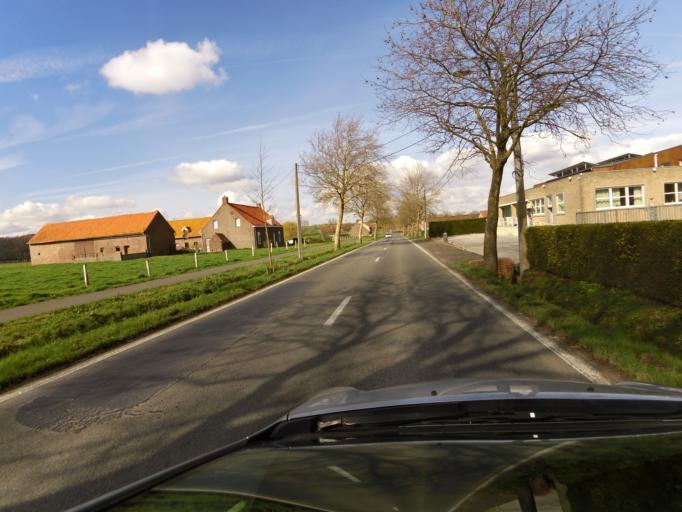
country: FR
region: Nord-Pas-de-Calais
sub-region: Departement du Nord
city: Nieppe
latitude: 50.7584
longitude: 2.8291
